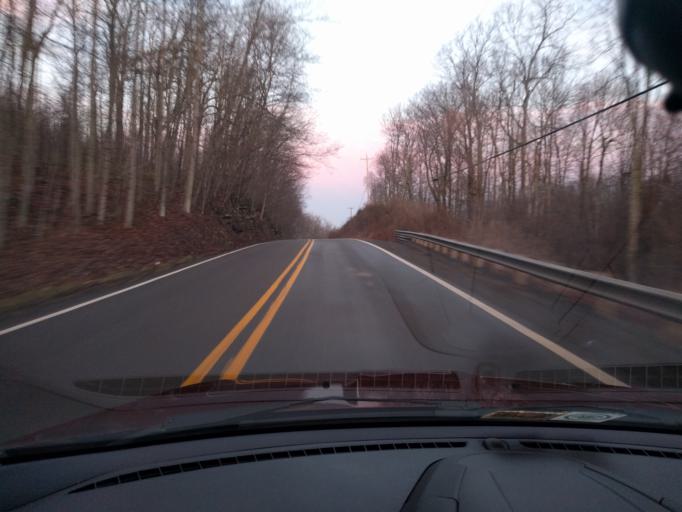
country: US
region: West Virginia
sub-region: Greenbrier County
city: Rainelle
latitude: 38.0156
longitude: -80.9037
